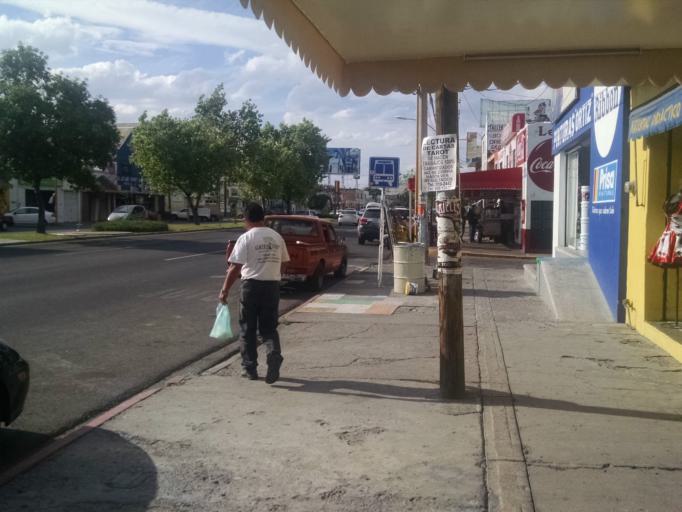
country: MX
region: Aguascalientes
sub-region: Aguascalientes
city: Aguascalientes
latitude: 21.8787
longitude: -102.3122
